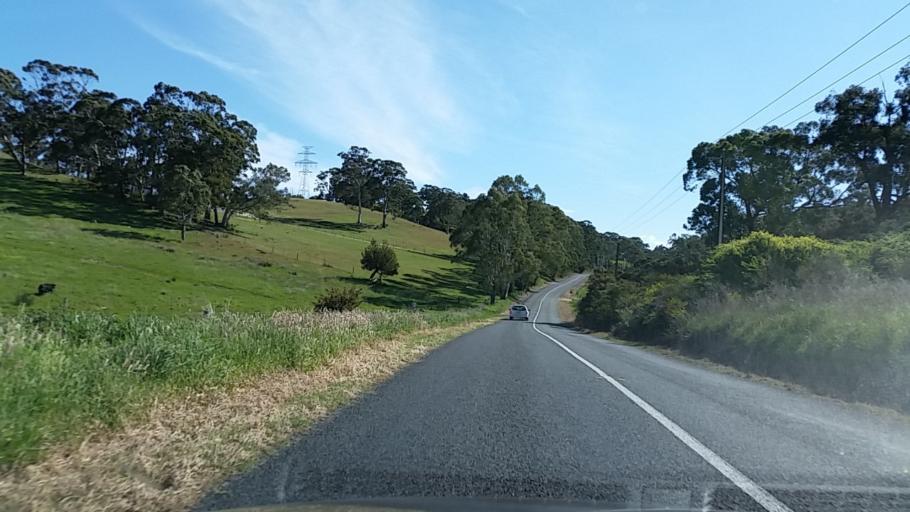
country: AU
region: South Australia
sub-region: Mount Barker
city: Little Hampton
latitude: -35.0782
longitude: 138.8314
